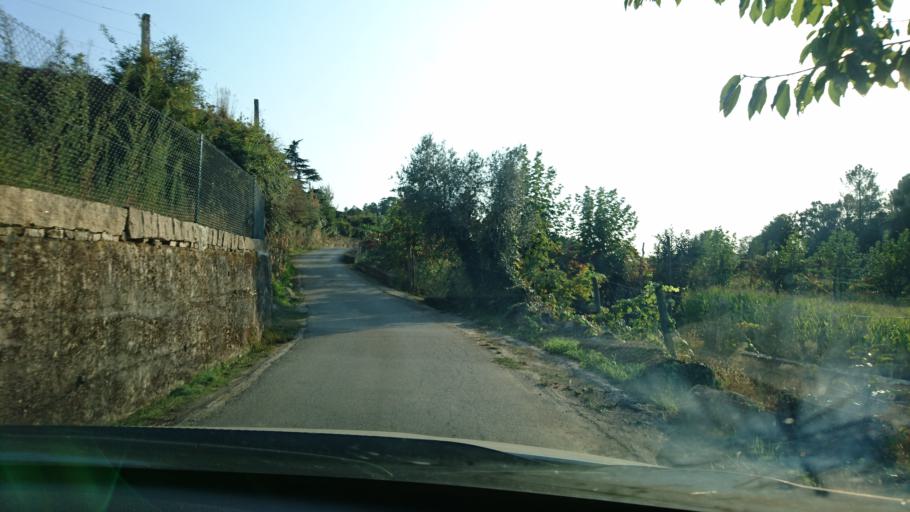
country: PT
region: Vila Real
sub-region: Mondim de Basto
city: Mondim de Basto
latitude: 41.4495
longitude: -7.9285
